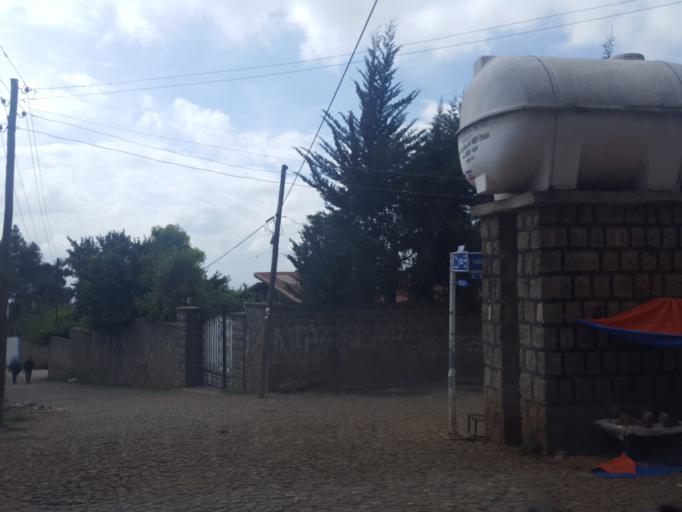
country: ET
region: Adis Abeba
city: Addis Ababa
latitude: 9.0653
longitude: 38.7459
